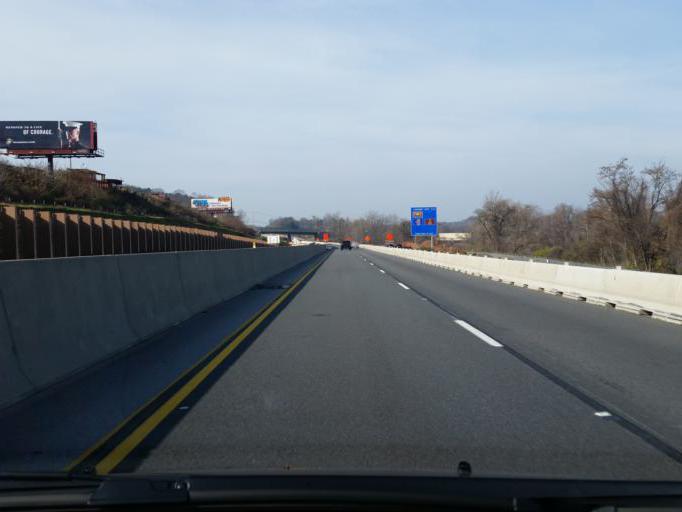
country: US
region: Pennsylvania
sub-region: Dauphin County
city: Steelton
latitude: 40.2030
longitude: -76.8461
